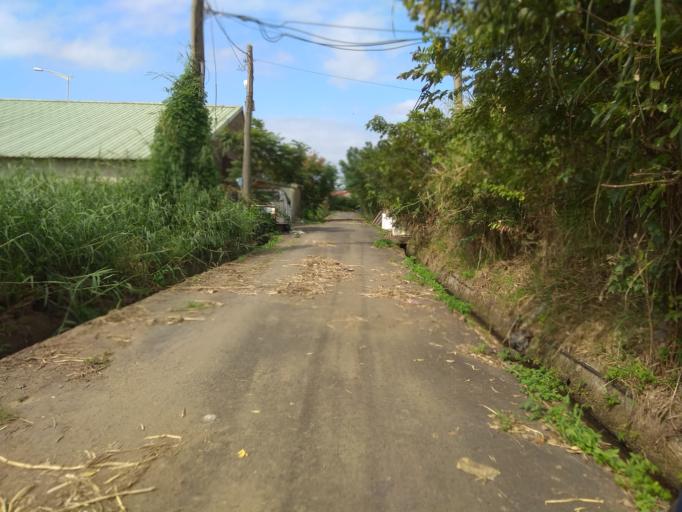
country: TW
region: Taiwan
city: Taoyuan City
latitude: 25.0542
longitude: 121.2157
